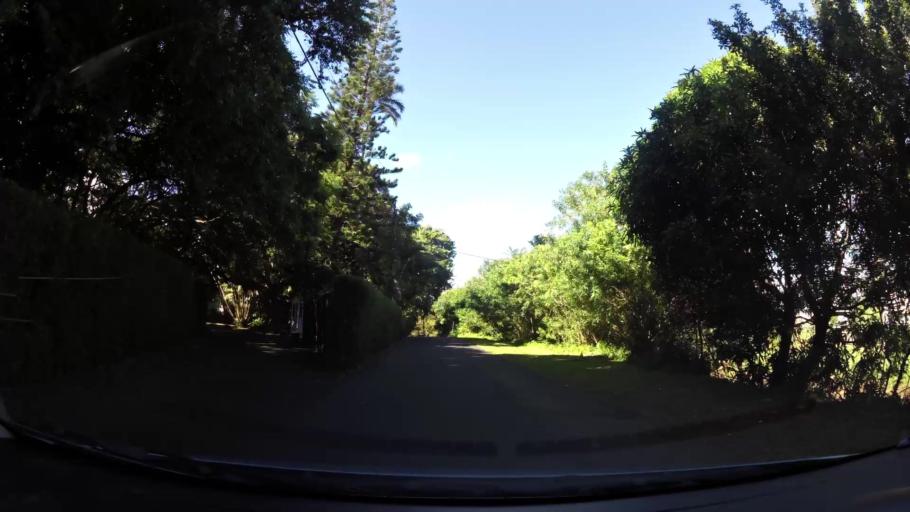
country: MU
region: Plaines Wilhems
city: Vacoas
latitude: -20.3006
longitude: 57.4950
